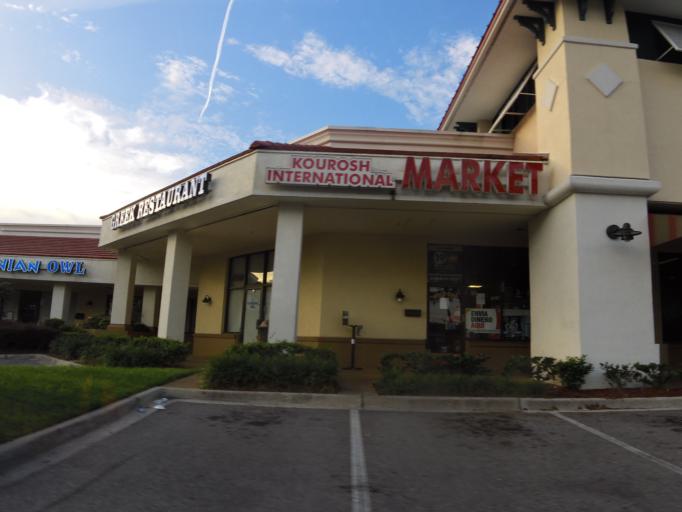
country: US
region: Florida
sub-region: Saint Johns County
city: Fruit Cove
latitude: 30.2217
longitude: -81.5590
